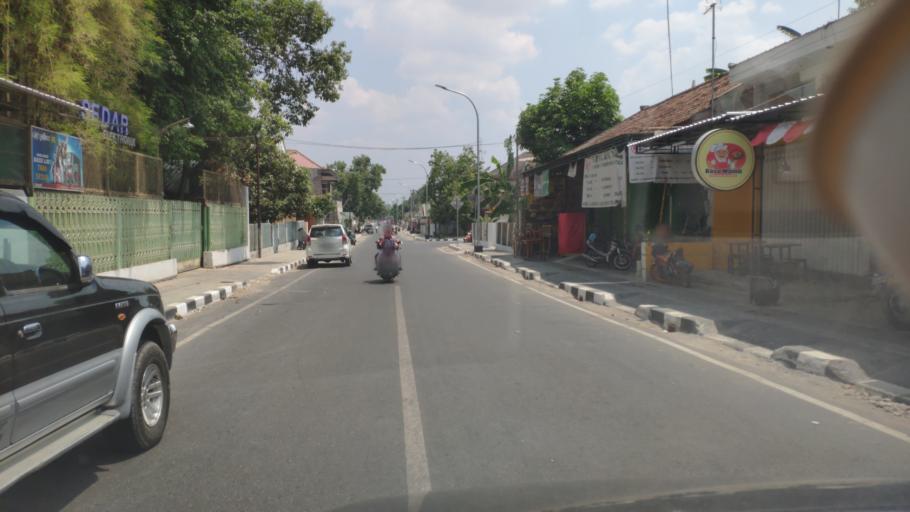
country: ID
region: Central Java
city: Tempelan
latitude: -6.9697
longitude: 111.4141
